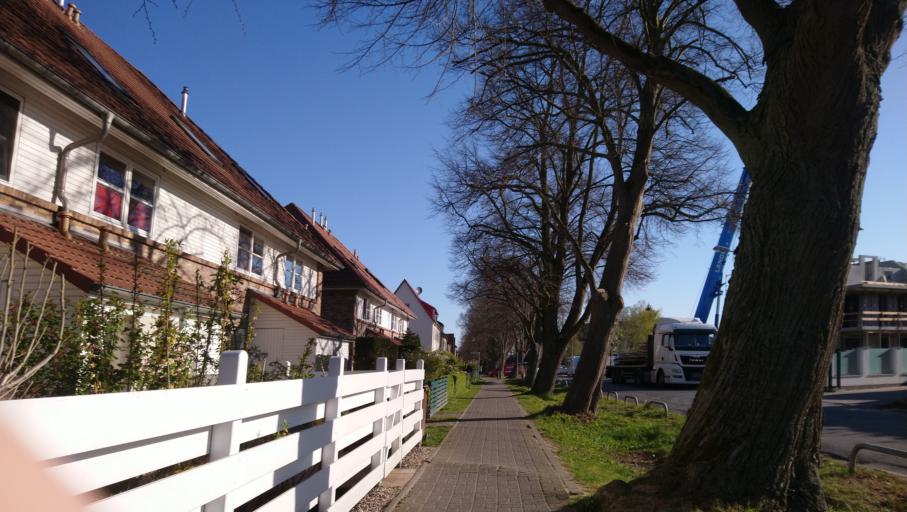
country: DE
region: Mecklenburg-Vorpommern
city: Rostock
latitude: 54.0685
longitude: 12.1343
